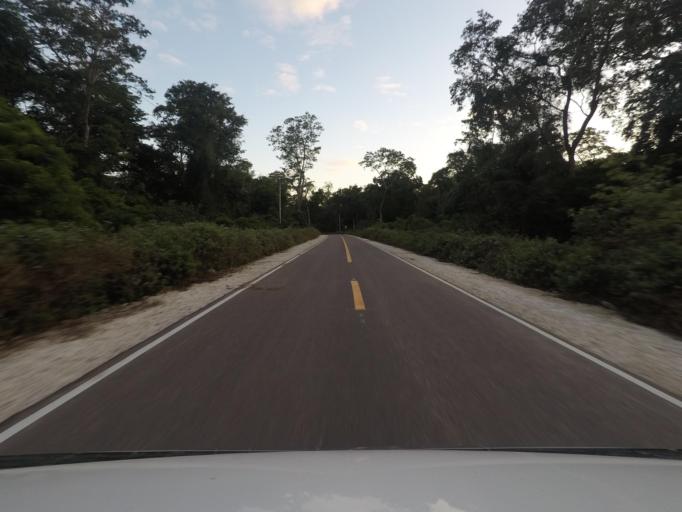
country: TL
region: Lautem
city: Lospalos
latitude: -8.4064
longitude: 127.2884
